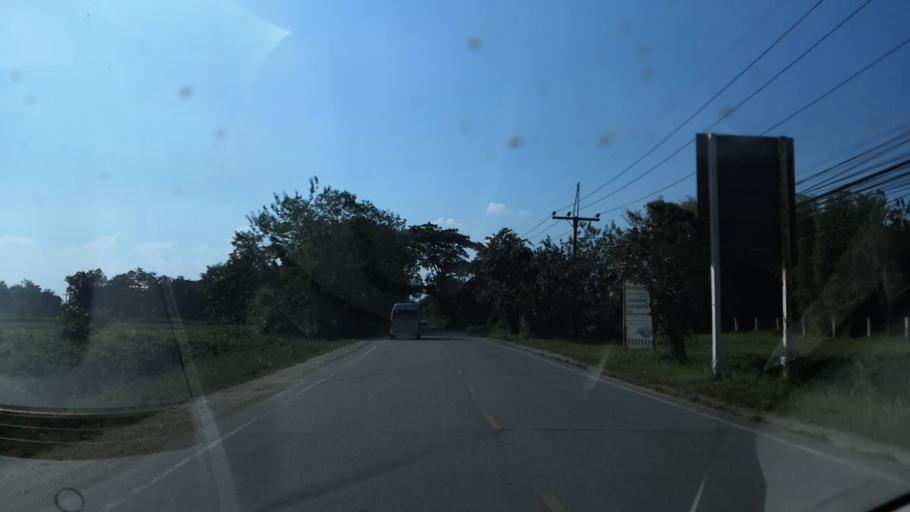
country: TH
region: Chiang Rai
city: Chiang Rai
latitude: 19.9294
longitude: 99.8575
